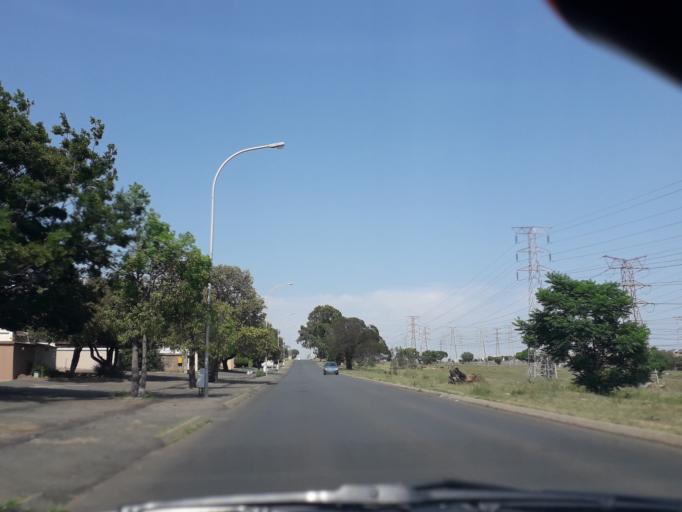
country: ZA
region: Gauteng
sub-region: City of Johannesburg Metropolitan Municipality
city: Modderfontein
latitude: -26.1214
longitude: 28.1683
